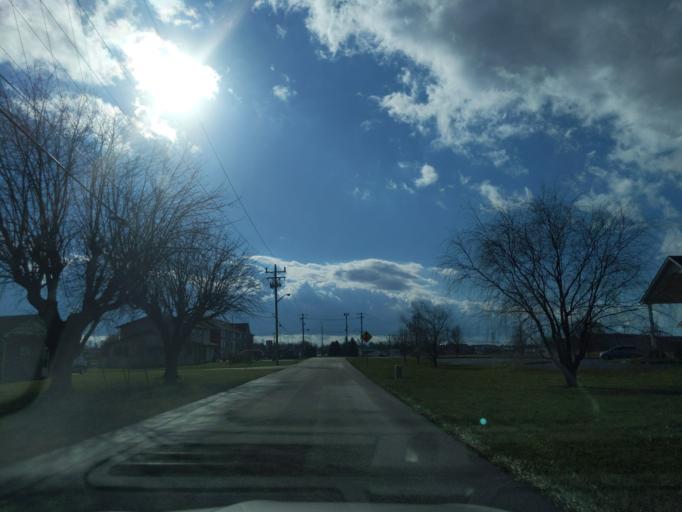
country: US
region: Indiana
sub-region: Decatur County
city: Greensburg
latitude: 39.3512
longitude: -85.4988
